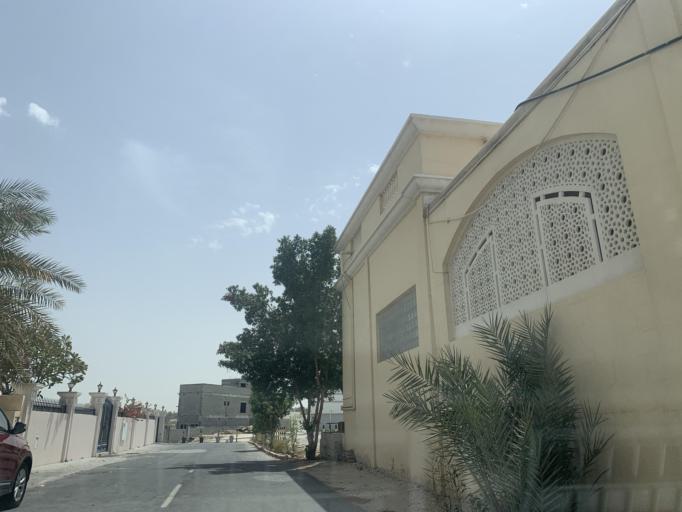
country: BH
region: Northern
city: Madinat `Isa
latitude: 26.1554
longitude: 50.5503
